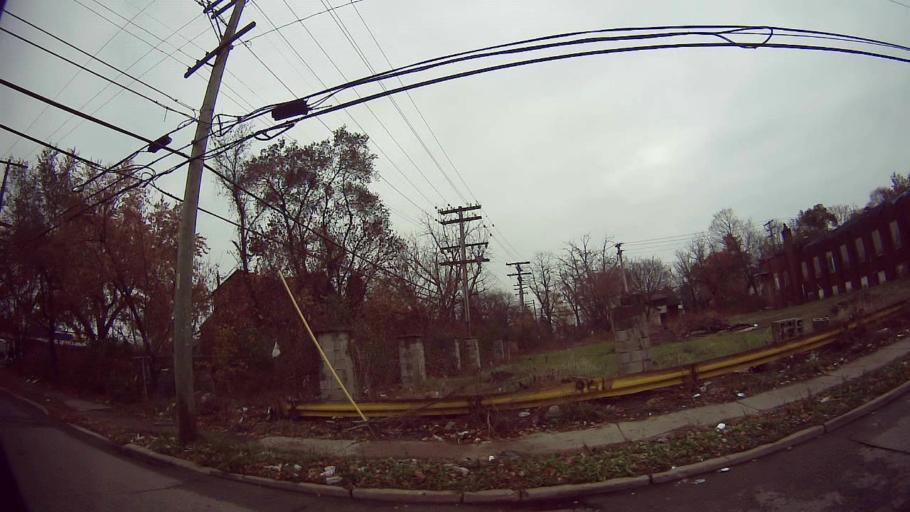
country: US
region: Michigan
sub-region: Wayne County
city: Redford
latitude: 42.4143
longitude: -83.2574
